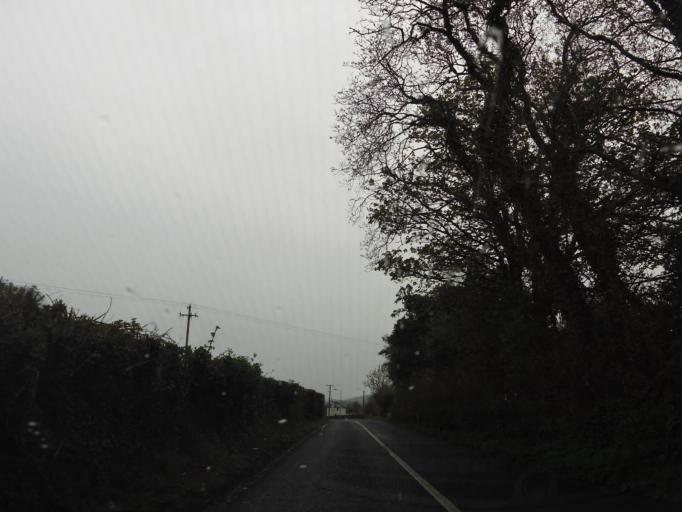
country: IE
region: Connaught
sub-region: Sligo
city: Collooney
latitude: 54.1752
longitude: -8.5071
